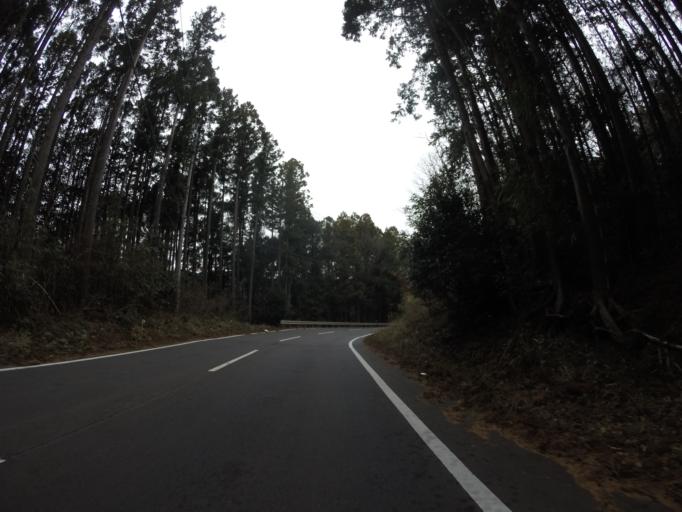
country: JP
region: Shizuoka
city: Fujinomiya
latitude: 35.2403
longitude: 138.5725
